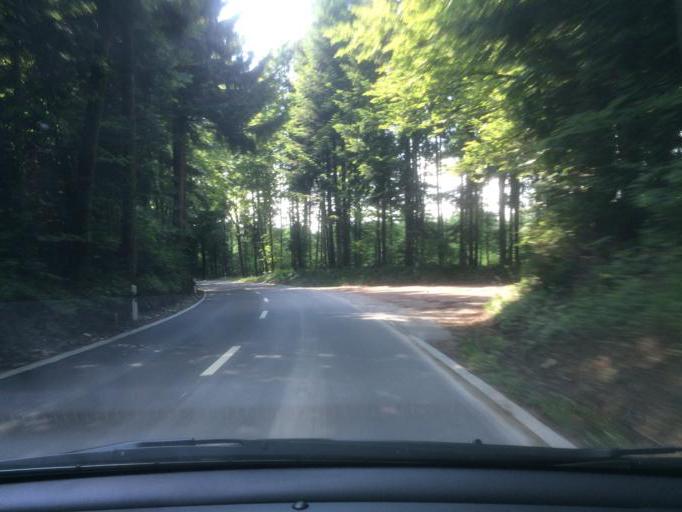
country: CH
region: Zurich
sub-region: Bezirk Uster
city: Uster / Ober-Uster
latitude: 47.3465
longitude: 8.7508
